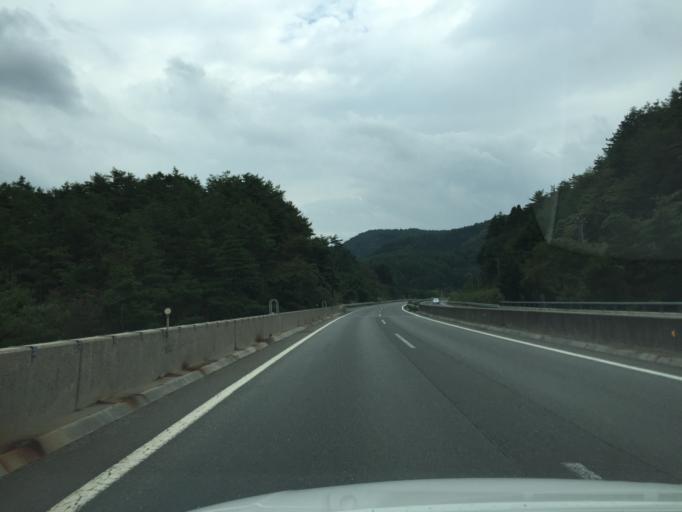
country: JP
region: Fukushima
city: Iwaki
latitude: 37.1331
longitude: 140.7534
